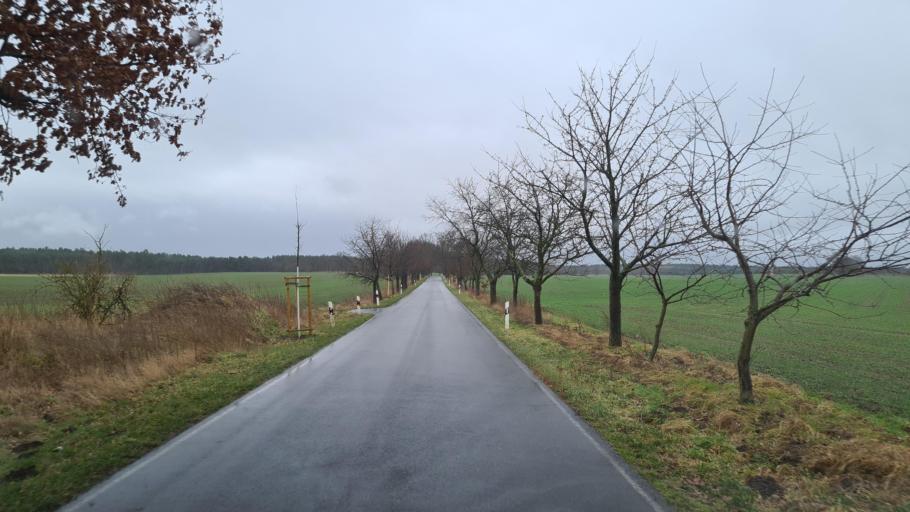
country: DE
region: Brandenburg
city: Gransee
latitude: 52.8963
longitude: 13.1998
